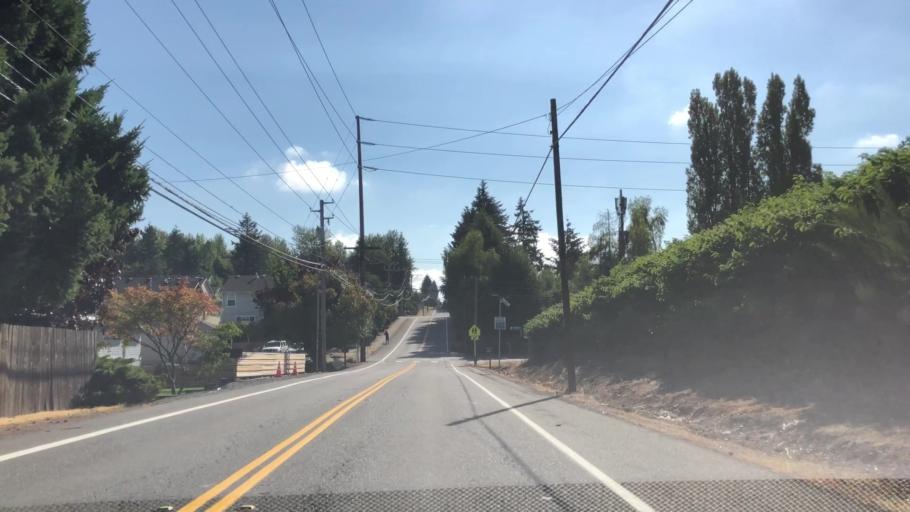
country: US
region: Washington
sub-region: King County
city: East Hill-Meridian
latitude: 47.4232
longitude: -122.2085
